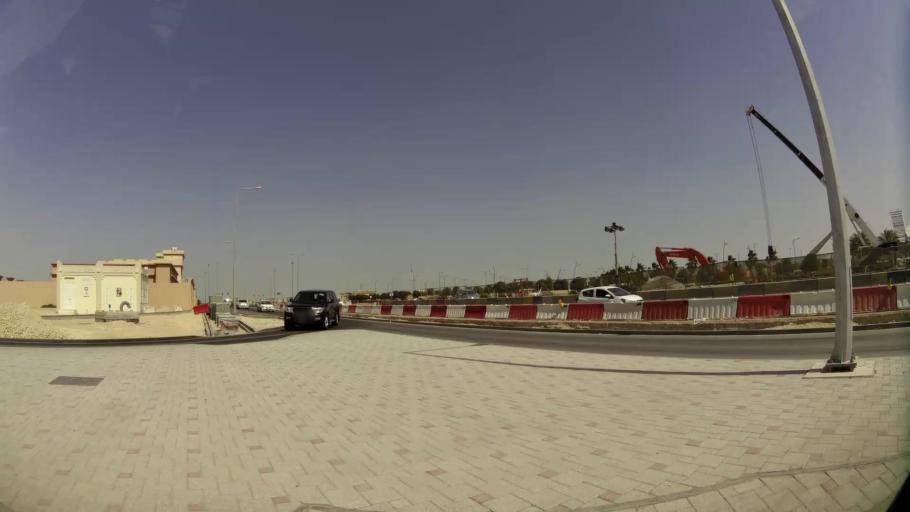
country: QA
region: Baladiyat Umm Salal
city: Umm Salal Muhammad
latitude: 25.3761
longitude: 51.4671
